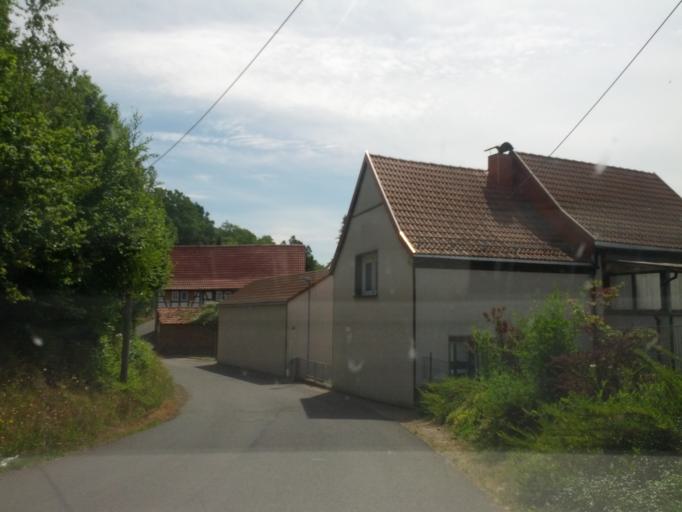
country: DE
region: Thuringia
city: Seebach
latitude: 50.9503
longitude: 10.4224
